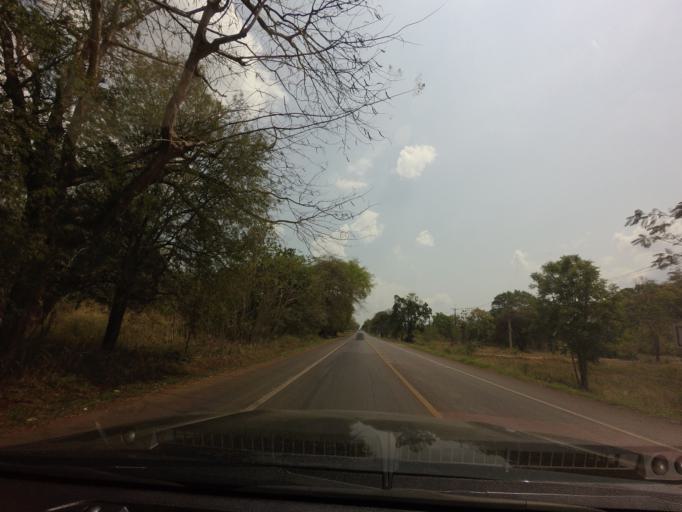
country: TH
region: Kanchanaburi
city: Sai Yok
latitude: 14.1353
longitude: 99.1539
